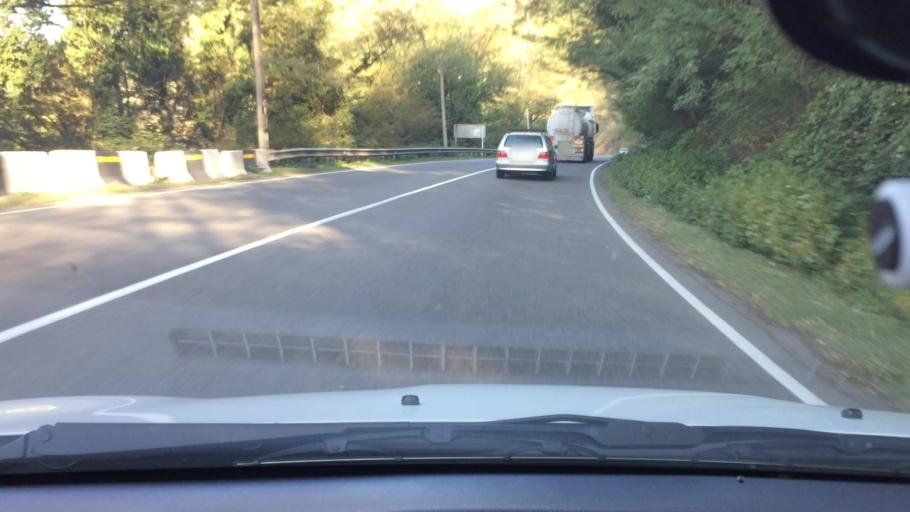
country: GE
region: Imereti
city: Kharagauli
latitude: 42.1005
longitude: 43.2278
